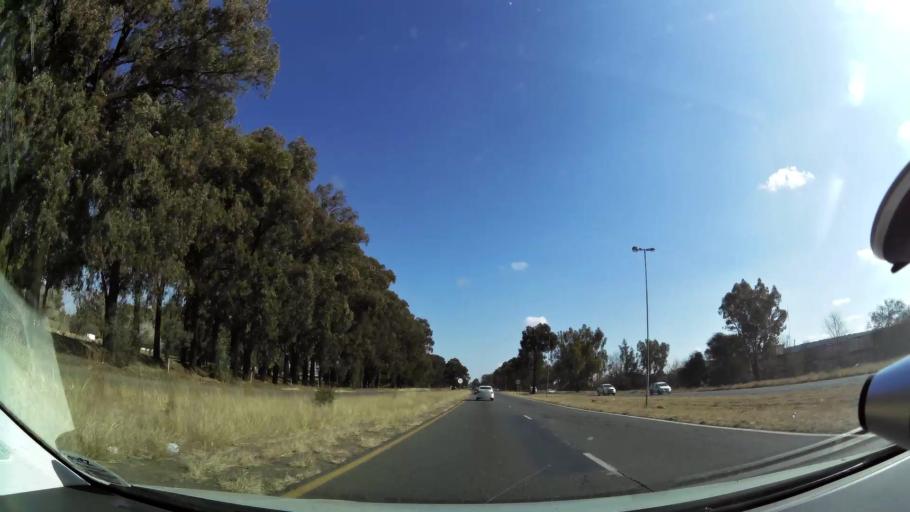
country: ZA
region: Orange Free State
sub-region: Mangaung Metropolitan Municipality
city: Bloemfontein
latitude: -29.1161
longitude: 26.2479
